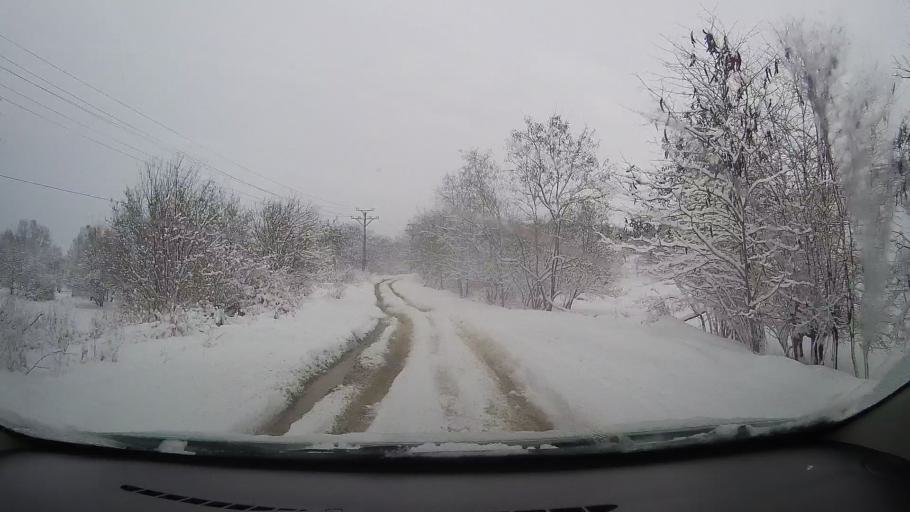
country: RO
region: Alba
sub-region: Comuna Pianu
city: Pianu de Jos
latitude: 45.9611
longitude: 23.4830
